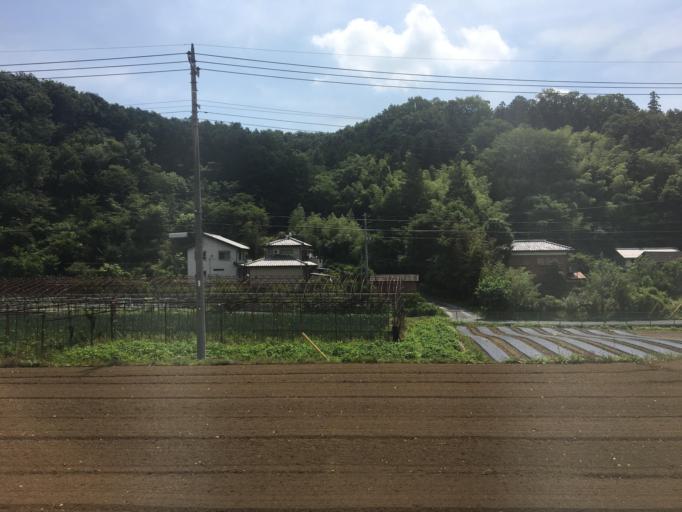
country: JP
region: Saitama
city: Ogawa
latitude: 36.0792
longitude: 139.2377
